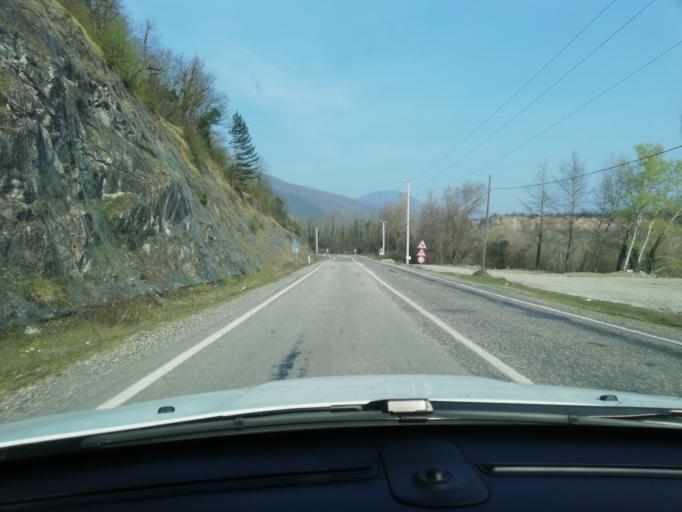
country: TR
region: Karabuk
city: Yenice
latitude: 41.2024
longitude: 32.3730
